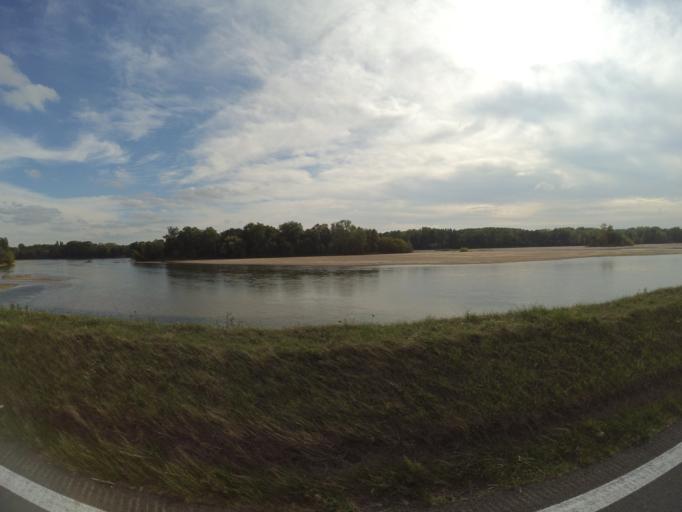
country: FR
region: Centre
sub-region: Departement d'Indre-et-Loire
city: La Chapelle-sur-Loire
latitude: 47.2431
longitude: 0.2062
